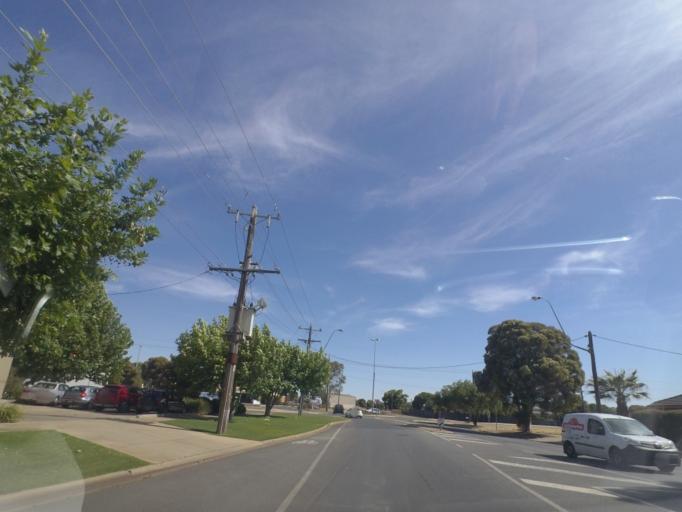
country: AU
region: Victoria
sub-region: Greater Shepparton
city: Shepparton
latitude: -36.3850
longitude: 145.4027
